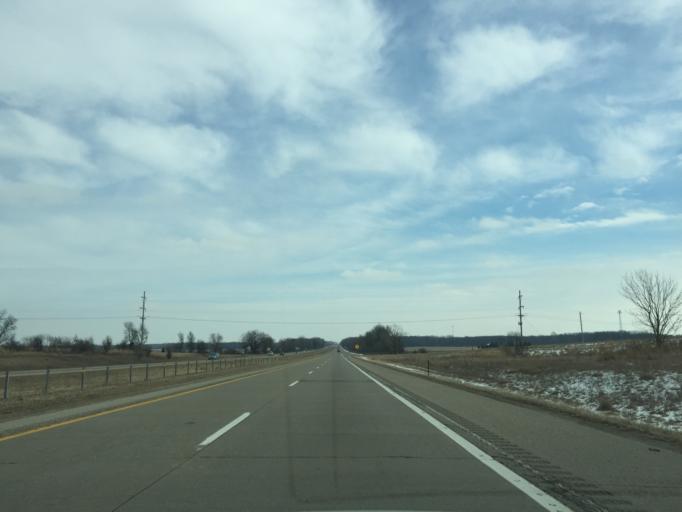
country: US
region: Michigan
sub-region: Ionia County
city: Saranac
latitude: 42.8793
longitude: -85.2441
